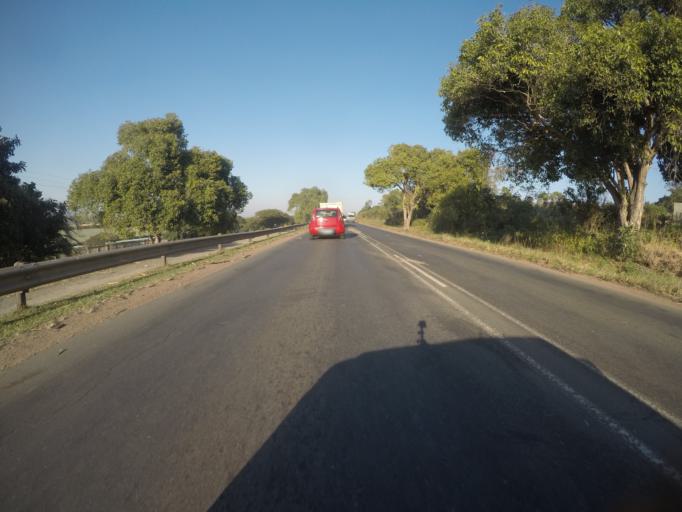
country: ZA
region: KwaZulu-Natal
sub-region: iLembe District Municipality
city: Stanger
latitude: -29.4051
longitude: 31.2494
